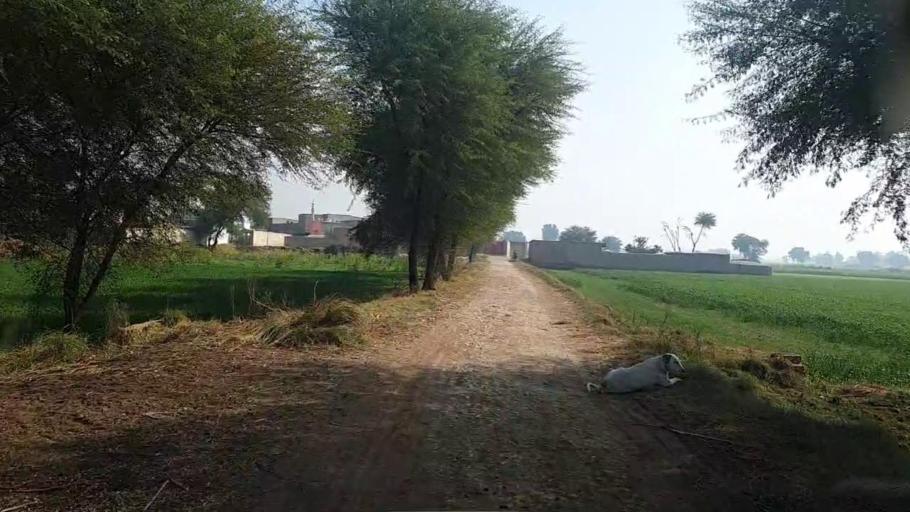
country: PK
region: Sindh
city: Khairpur
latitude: 27.9424
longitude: 69.6763
